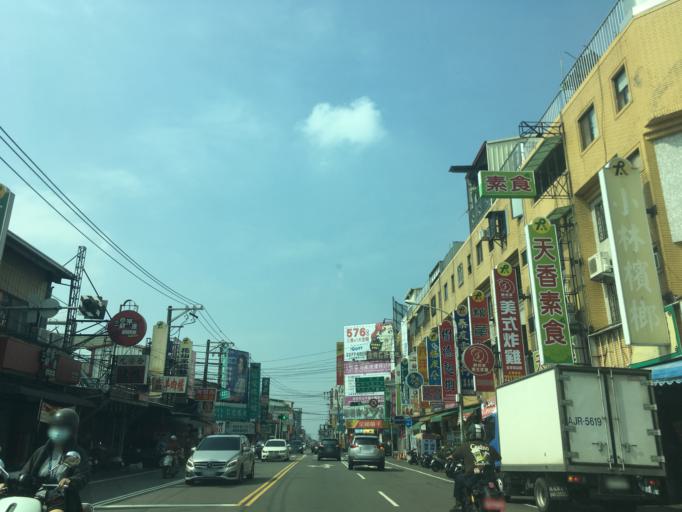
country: TW
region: Taiwan
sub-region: Taichung City
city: Taichung
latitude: 24.1504
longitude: 120.7107
